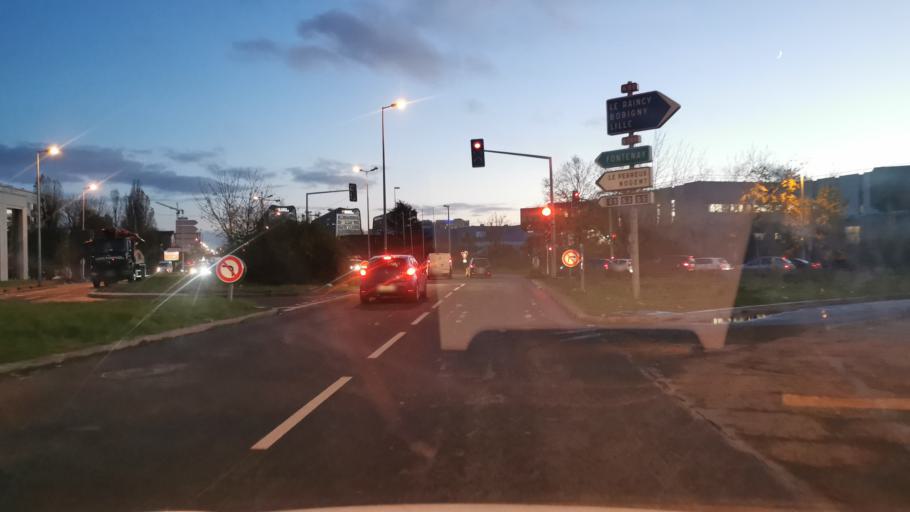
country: FR
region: Ile-de-France
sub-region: Departement du Val-de-Marne
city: Fontenay-sous-Bois
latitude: 48.8602
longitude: 2.4902
